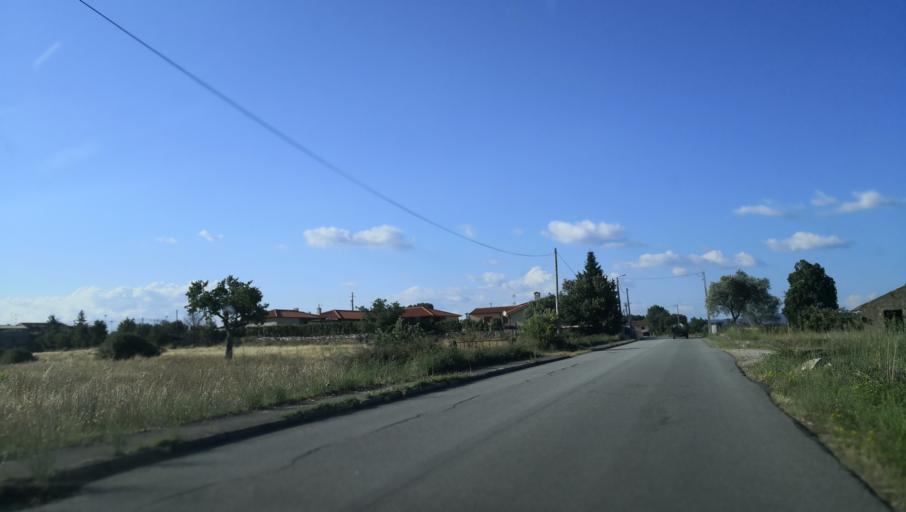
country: PT
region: Vila Real
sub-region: Chaves
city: Chaves
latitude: 41.7744
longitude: -7.4466
